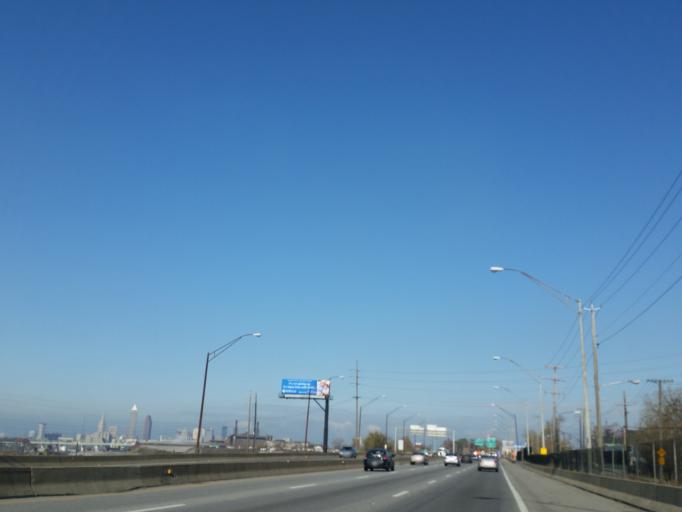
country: US
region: Ohio
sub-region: Cuyahoga County
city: Newburgh Heights
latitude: 41.4615
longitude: -81.6569
